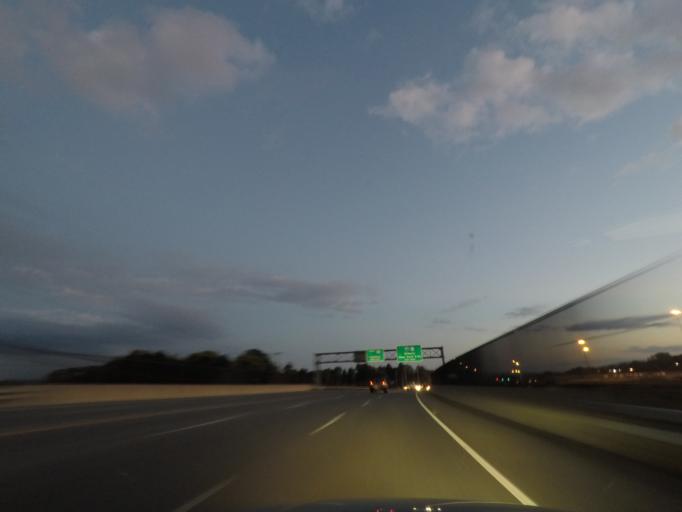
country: US
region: New York
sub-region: Orange County
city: Gardnertown
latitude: 41.5147
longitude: -74.0670
